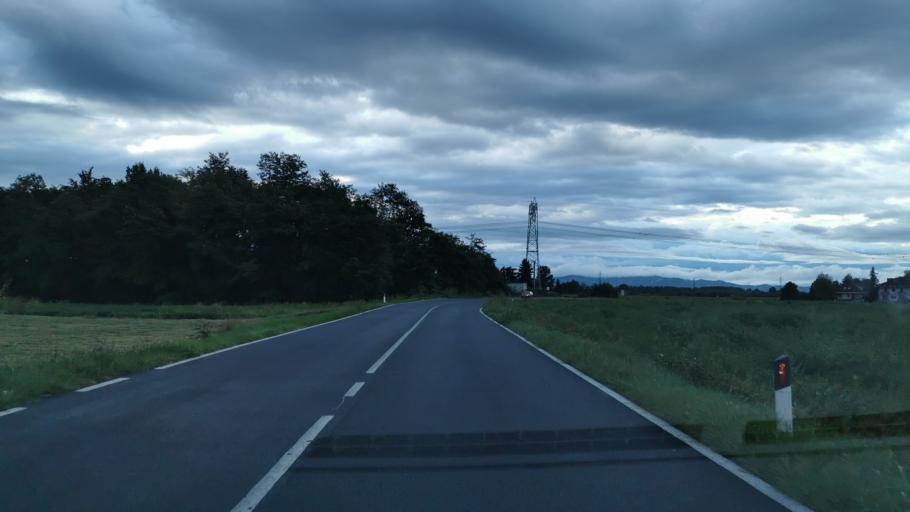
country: IT
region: Piedmont
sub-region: Provincia di Torino
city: Lombardore
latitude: 45.2278
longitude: 7.7573
